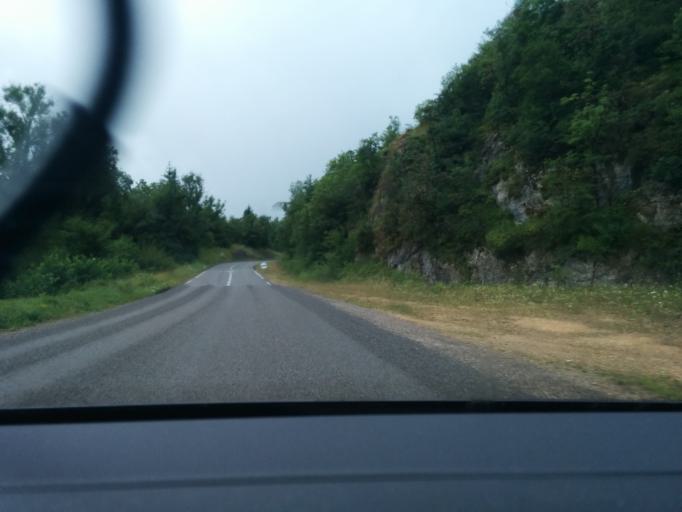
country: FR
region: Franche-Comte
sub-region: Departement du Jura
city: Saint-Lupicin
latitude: 46.4213
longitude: 5.8030
